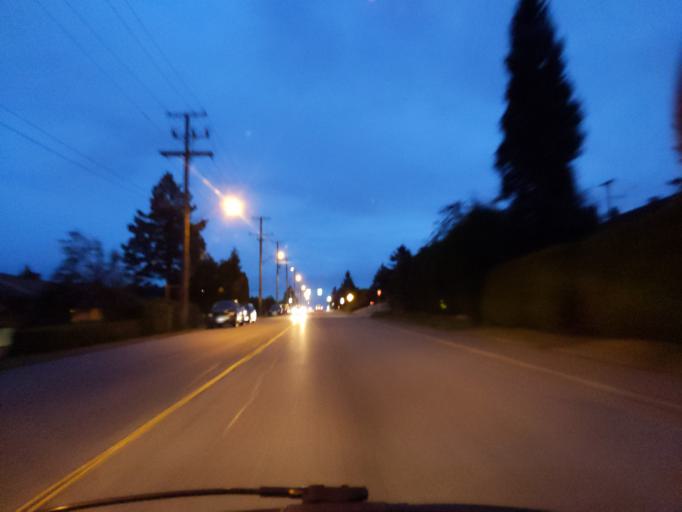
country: CA
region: British Columbia
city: New Westminster
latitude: 49.2274
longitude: -122.9028
